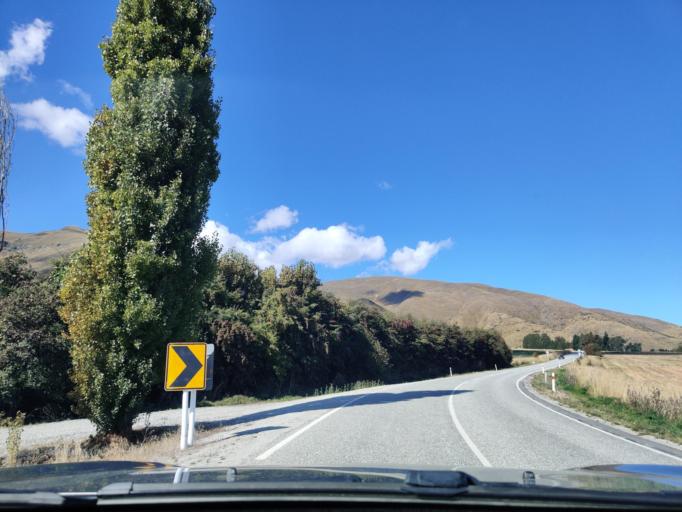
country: NZ
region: Otago
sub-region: Queenstown-Lakes District
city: Arrowtown
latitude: -44.9736
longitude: 168.8848
